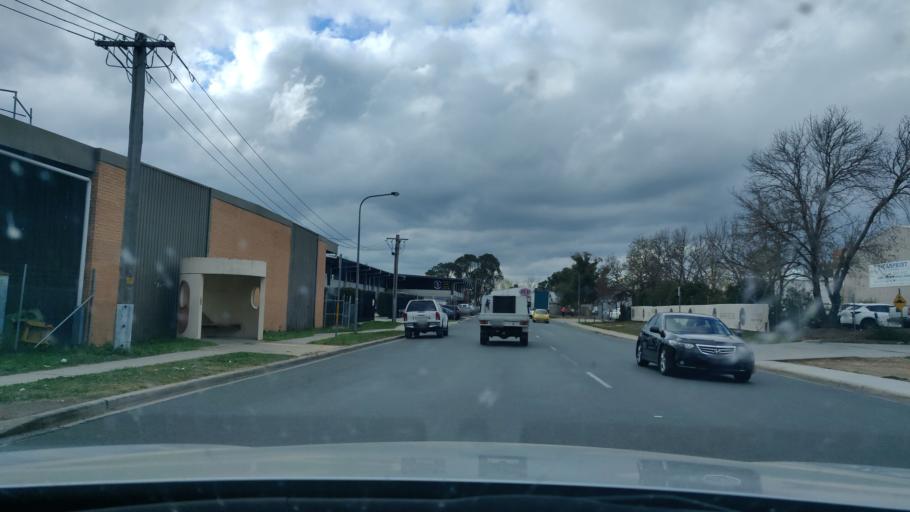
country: AU
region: Australian Capital Territory
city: Forrest
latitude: -35.3253
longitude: 149.1552
